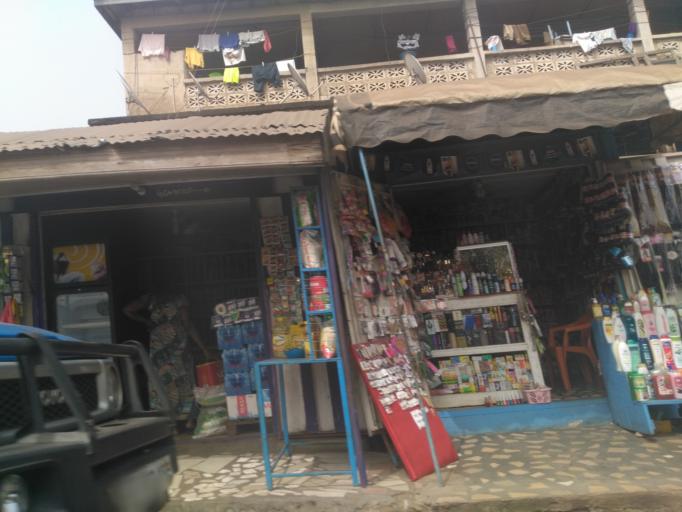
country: GH
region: Ashanti
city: Tafo
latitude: 6.7113
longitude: -1.6142
